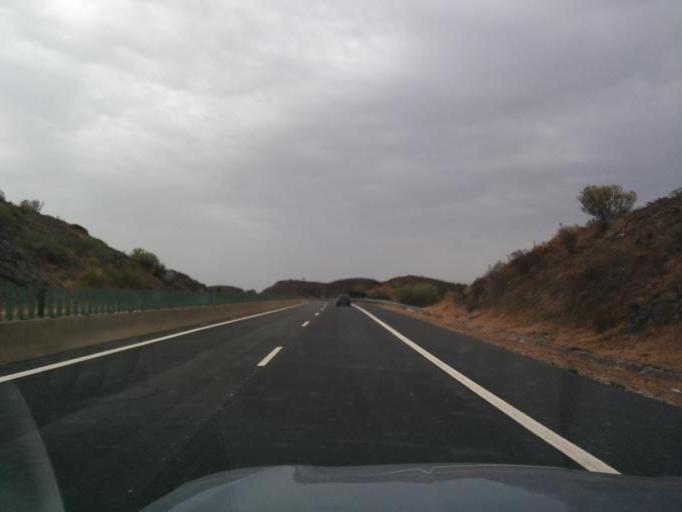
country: PT
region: Faro
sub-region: Tavira
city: Tavira
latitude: 37.1631
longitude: -7.6547
